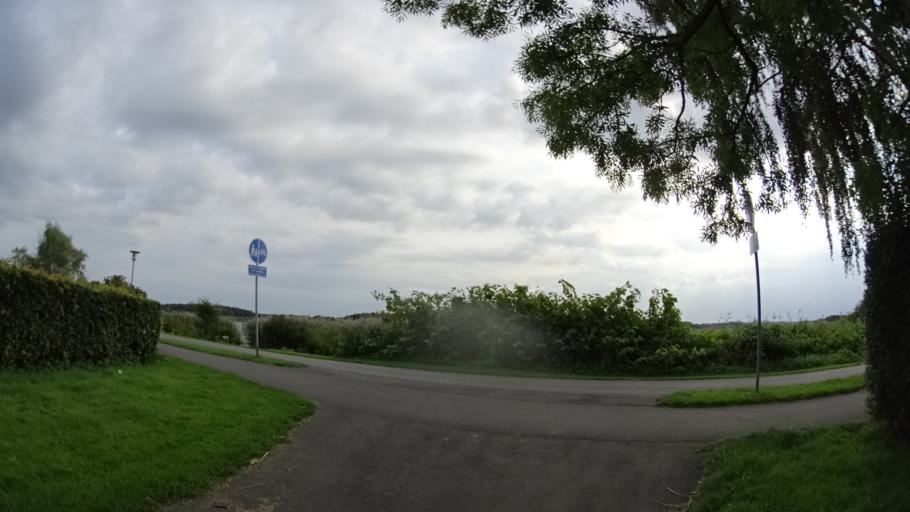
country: DK
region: Central Jutland
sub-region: Arhus Kommune
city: Stavtrup
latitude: 56.1506
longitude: 10.1047
